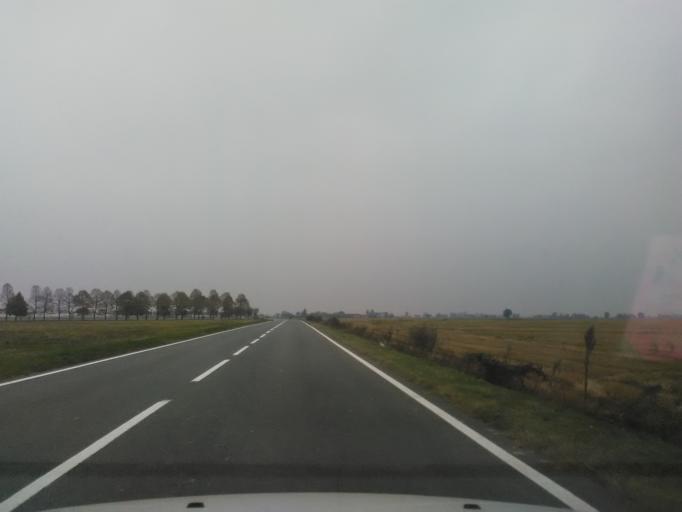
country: IT
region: Piedmont
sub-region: Provincia di Vercelli
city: Ronsecco
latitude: 45.2597
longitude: 8.2325
